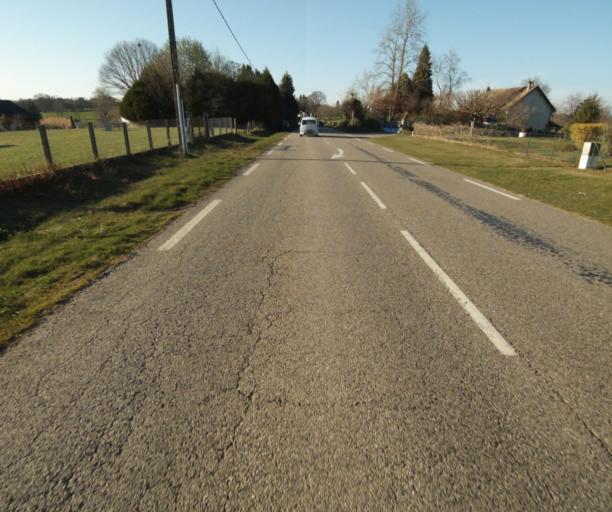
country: FR
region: Limousin
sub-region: Departement de la Correze
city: Seilhac
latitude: 45.3767
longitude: 1.7241
